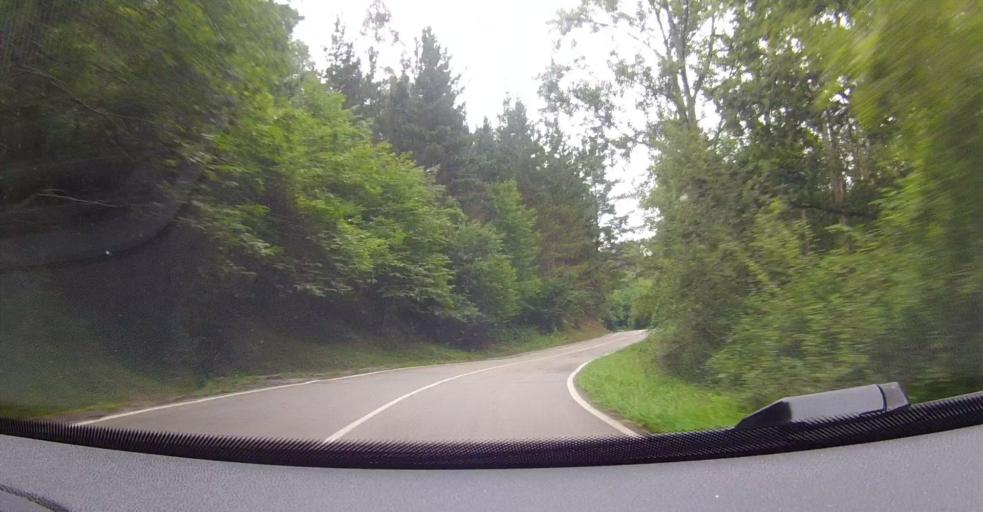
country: ES
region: Basque Country
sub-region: Bizkaia
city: Balmaseda
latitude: 43.2421
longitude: -3.2878
